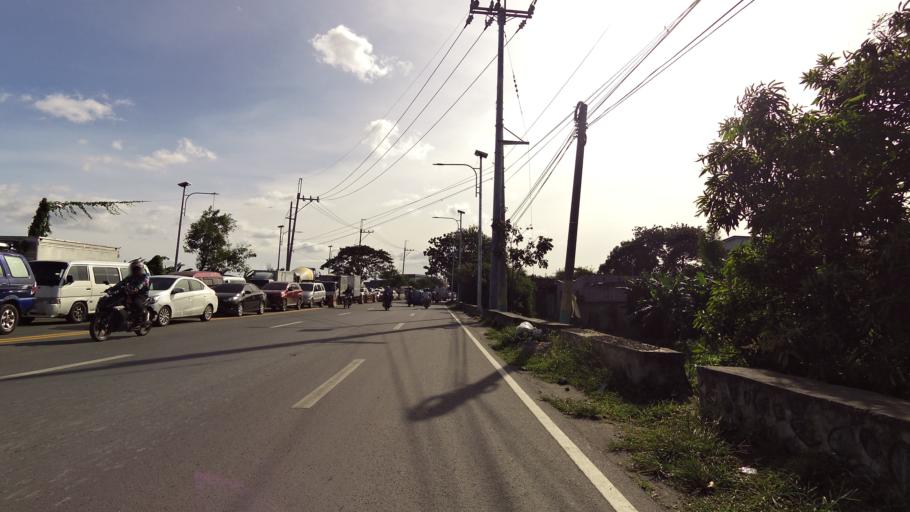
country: PH
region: Calabarzon
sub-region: Province of Rizal
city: Taytay
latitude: 14.5451
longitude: 121.1166
